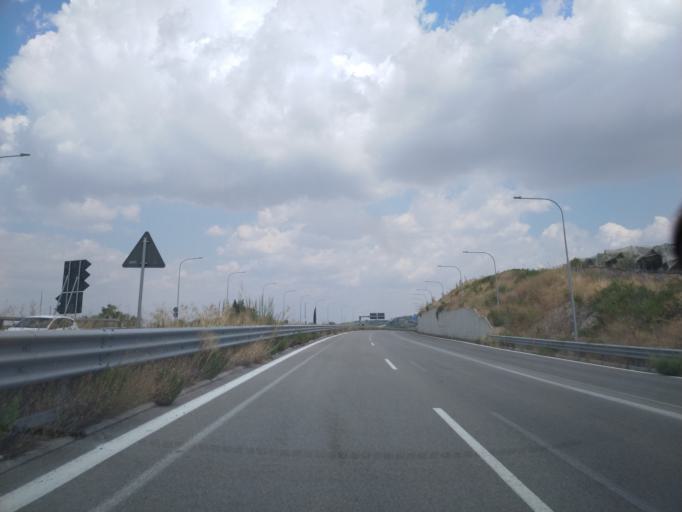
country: IT
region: Sicily
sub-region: Agrigento
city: Canicatti
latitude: 37.3830
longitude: 13.8129
